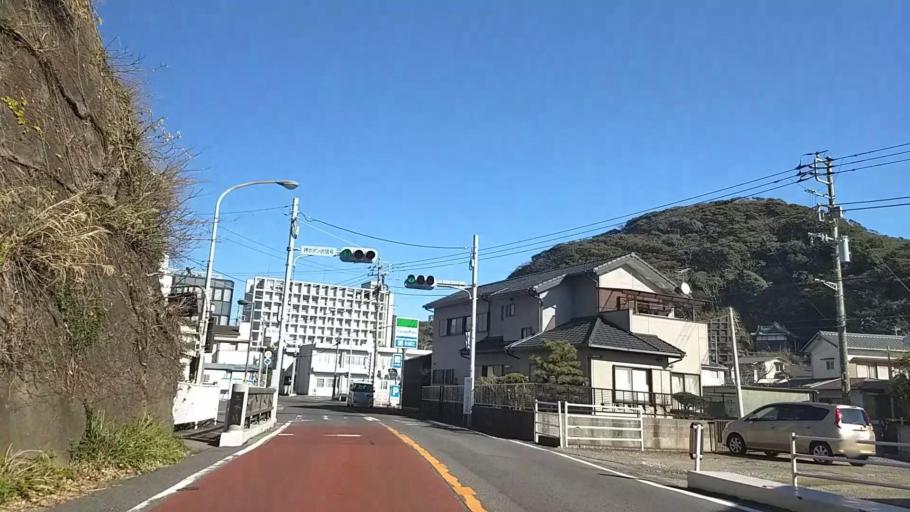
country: JP
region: Chiba
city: Katsuura
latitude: 35.1502
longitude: 140.3156
